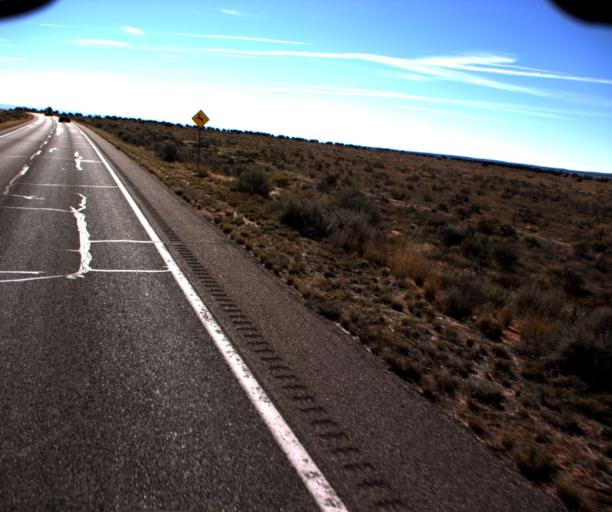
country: US
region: Arizona
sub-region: Mohave County
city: Colorado City
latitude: 36.8853
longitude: -112.9042
